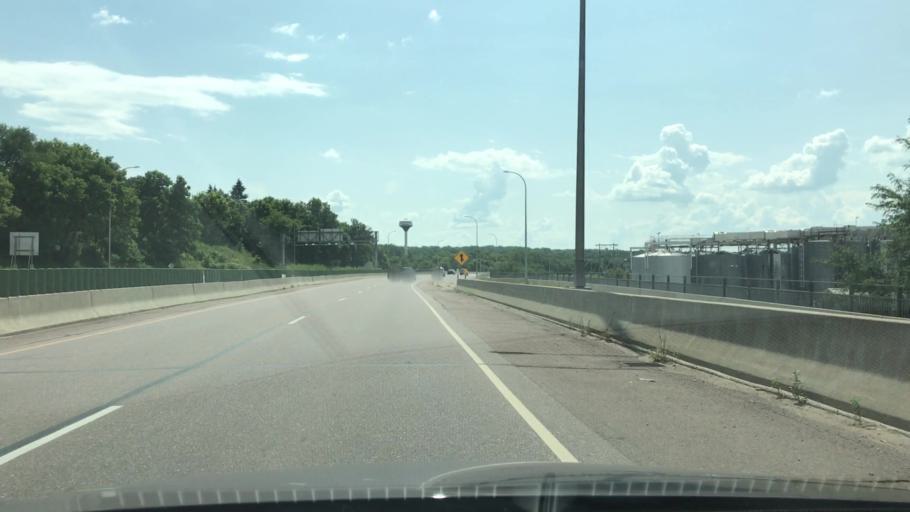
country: US
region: Minnesota
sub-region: Nicollet County
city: North Mankato
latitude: 44.1558
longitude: -94.0299
